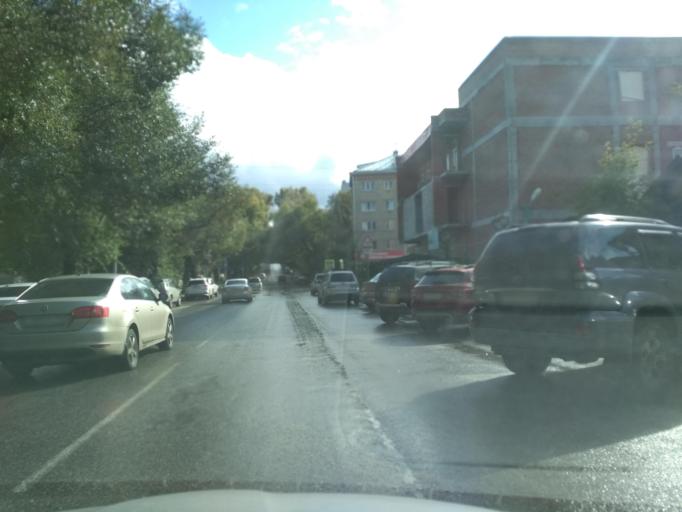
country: RU
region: Tomsk
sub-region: Tomskiy Rayon
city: Tomsk
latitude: 56.4822
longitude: 84.9515
